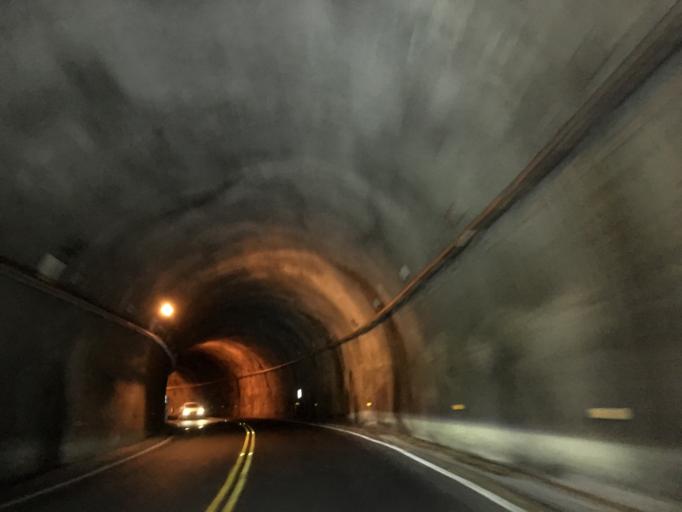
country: TW
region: Taiwan
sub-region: Hualien
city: Hualian
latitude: 24.2121
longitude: 121.4834
